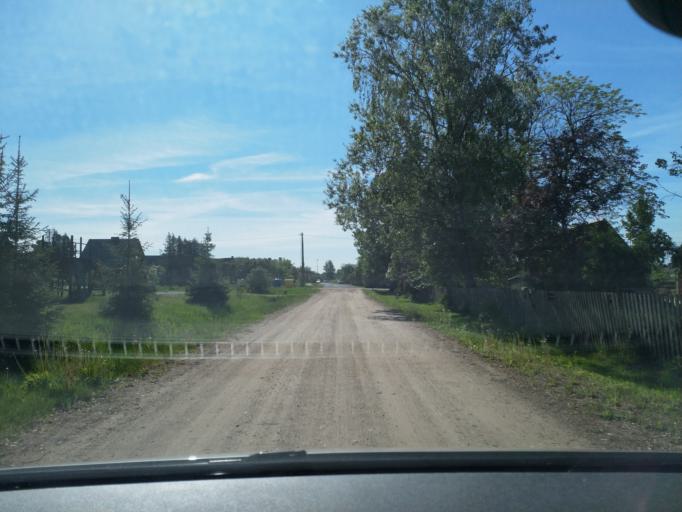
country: LV
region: Kuldigas Rajons
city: Kuldiga
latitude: 56.9768
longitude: 21.9831
